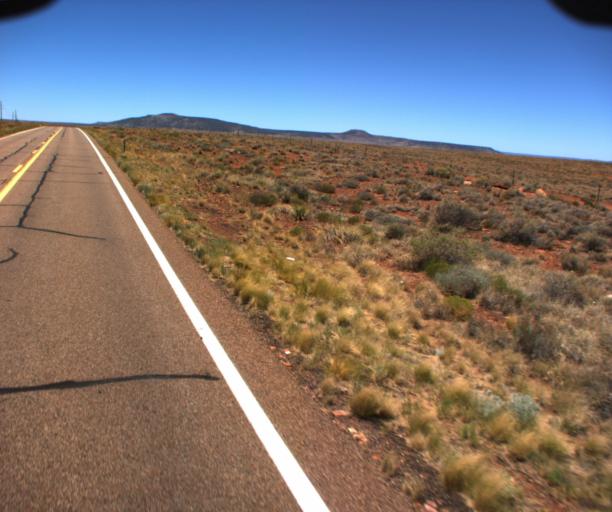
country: US
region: Arizona
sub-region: Coconino County
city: LeChee
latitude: 34.9177
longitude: -110.8247
